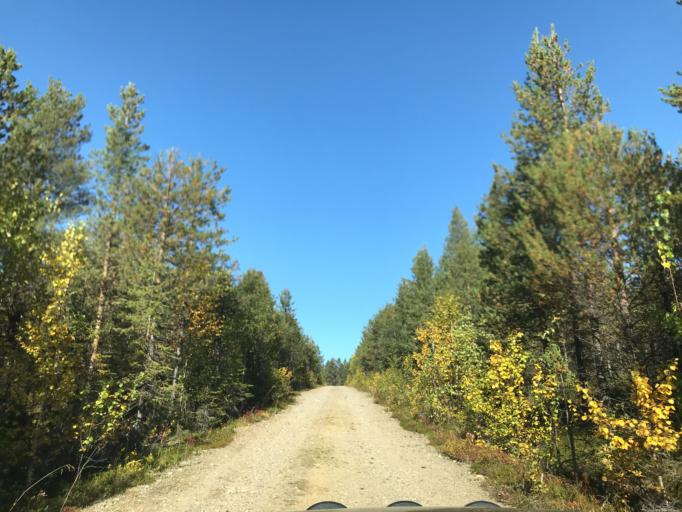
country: SE
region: Norrbotten
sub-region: Gallivare Kommun
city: Malmberget
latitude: 67.6481
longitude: 21.0837
